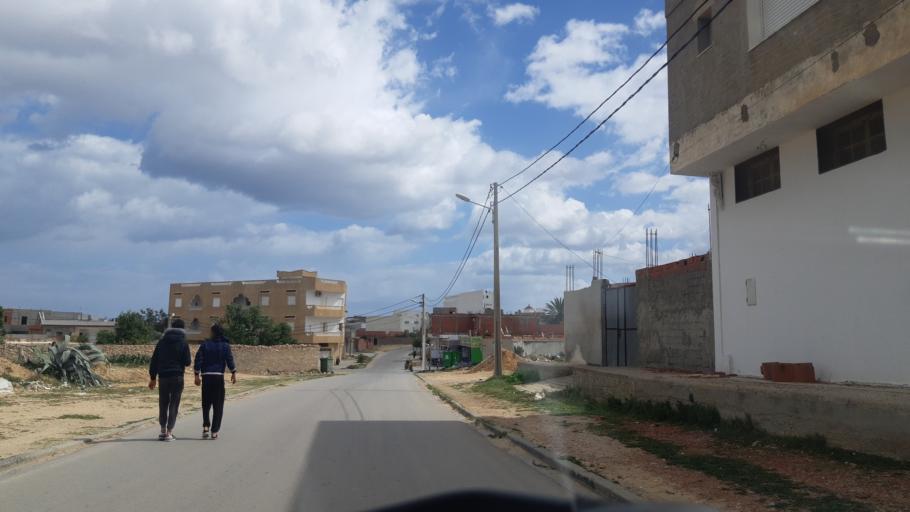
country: TN
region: Susah
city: Akouda
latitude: 35.8631
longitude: 10.5348
